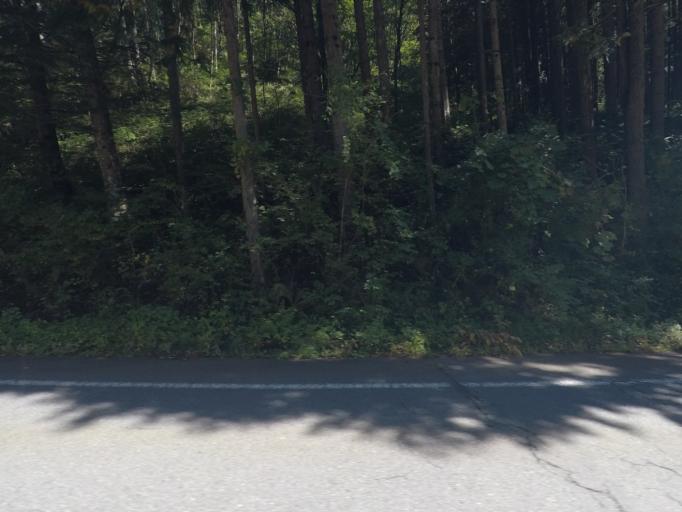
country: JP
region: Nagano
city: Shiojiri
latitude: 35.9961
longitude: 137.7390
